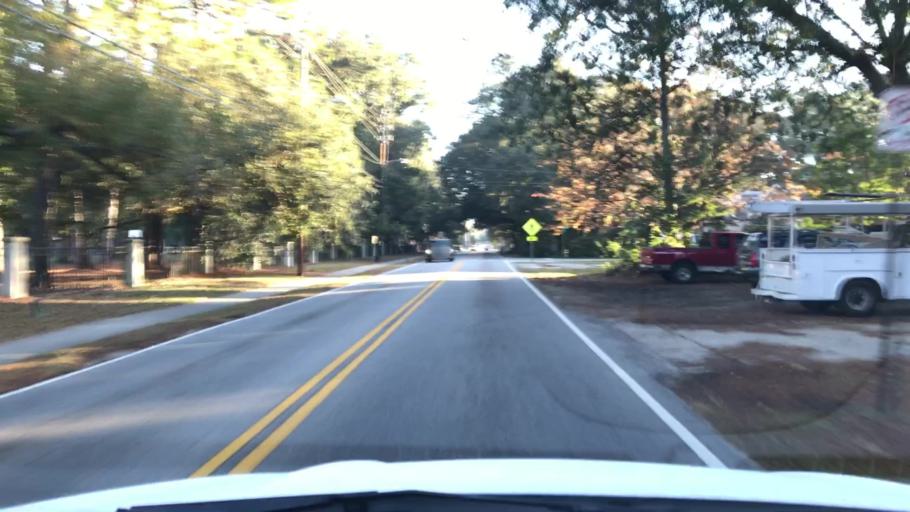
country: US
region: South Carolina
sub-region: Charleston County
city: North Charleston
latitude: 32.8165
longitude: -79.9998
